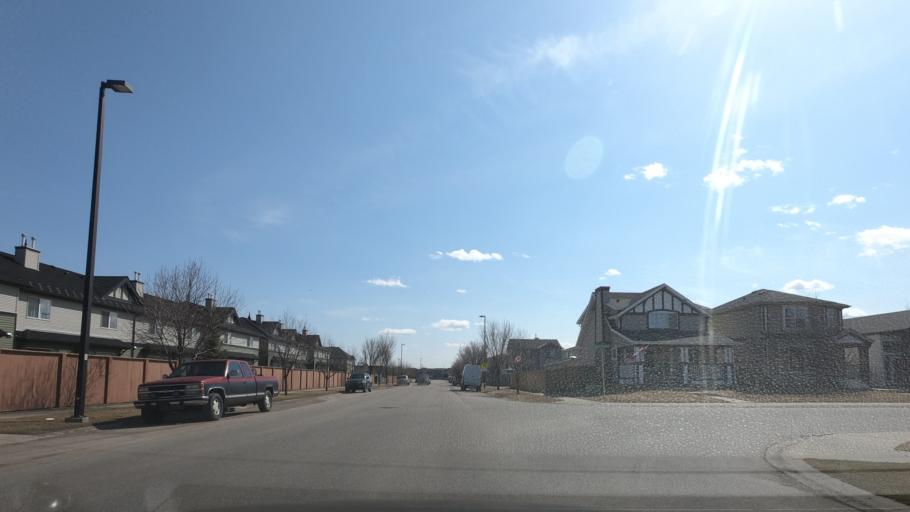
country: CA
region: Alberta
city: Airdrie
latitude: 51.2915
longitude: -114.0425
